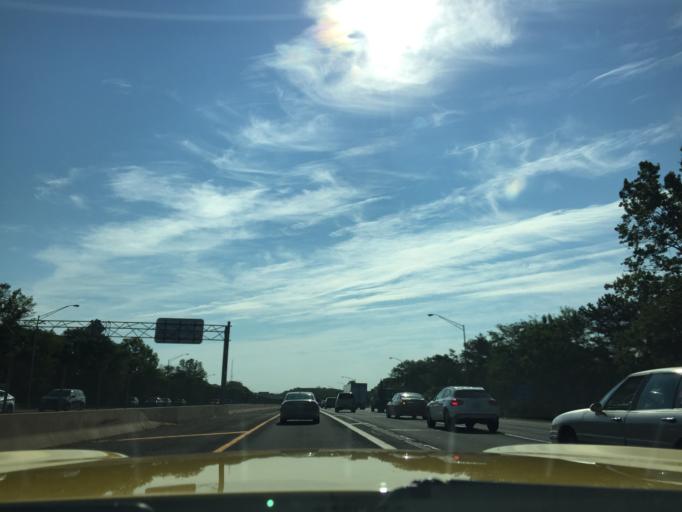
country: US
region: New York
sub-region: Suffolk County
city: Brentwood
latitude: 40.8059
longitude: -73.2427
